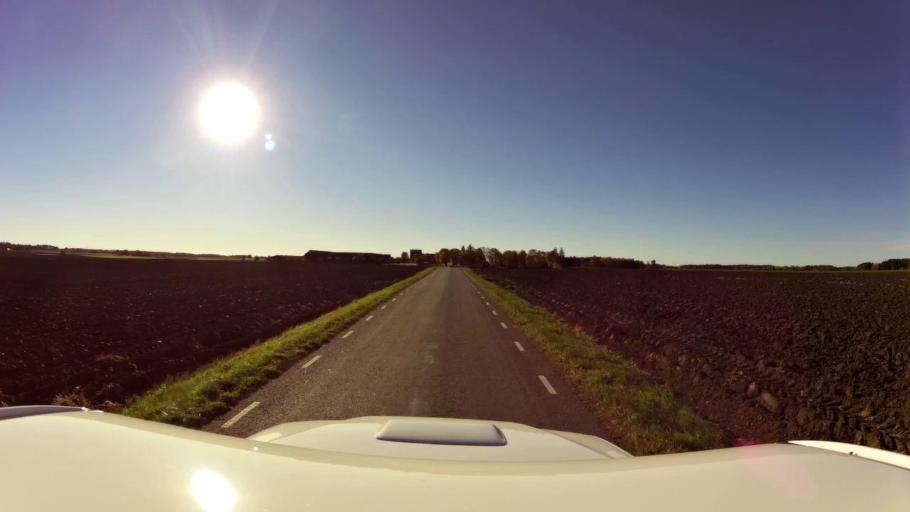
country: SE
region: OEstergoetland
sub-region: Linkopings Kommun
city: Ljungsbro
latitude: 58.5143
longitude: 15.4182
